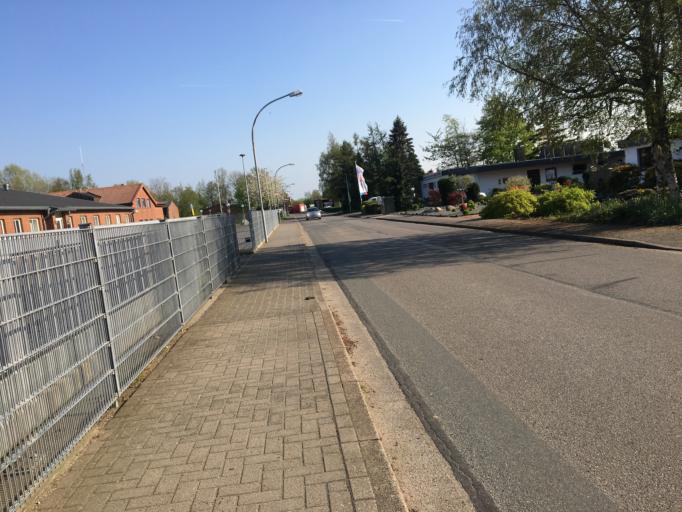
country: DE
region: Schleswig-Holstein
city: Tonning
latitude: 54.3222
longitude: 8.9532
